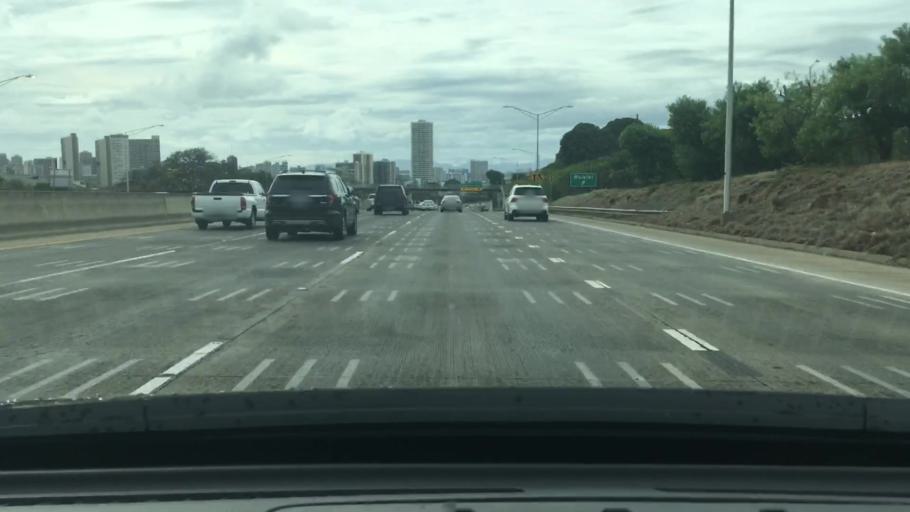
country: US
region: Hawaii
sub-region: Honolulu County
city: Honolulu
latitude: 21.2843
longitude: -157.8078
